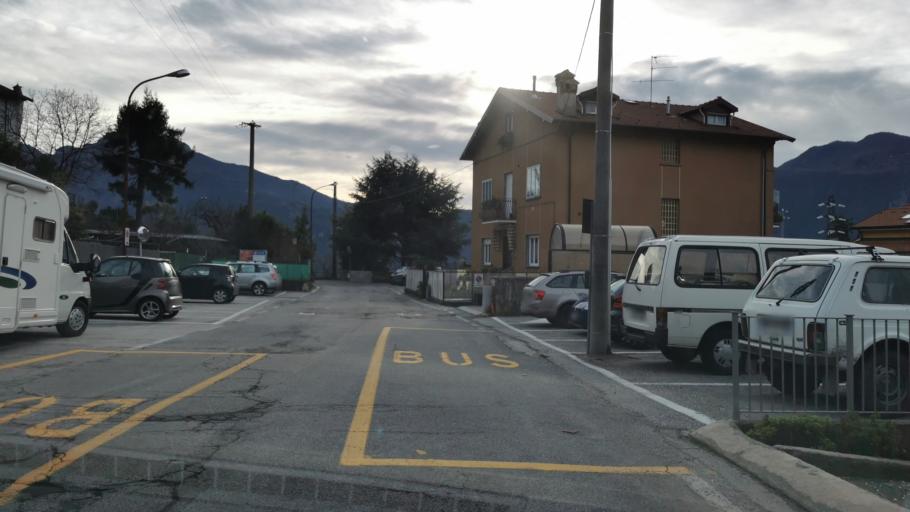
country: IT
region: Lombardy
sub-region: Provincia di Lecco
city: Mandello del Lario
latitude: 45.9226
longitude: 9.3274
